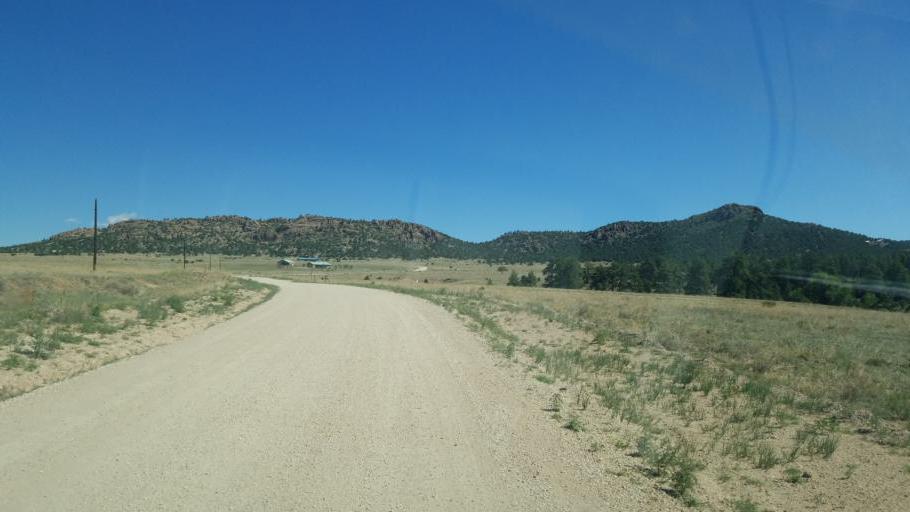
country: US
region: Colorado
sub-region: Custer County
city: Westcliffe
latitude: 38.2234
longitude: -105.4580
